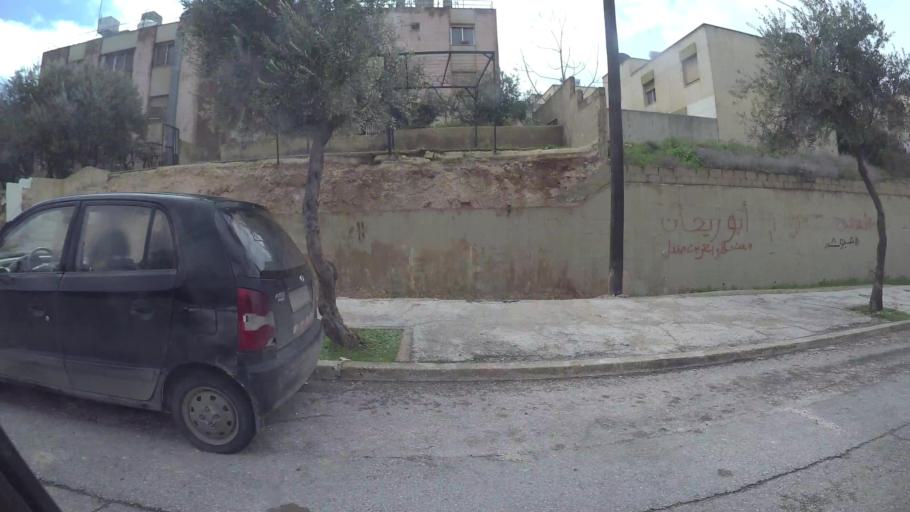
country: JO
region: Amman
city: Al Jubayhah
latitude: 32.0586
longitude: 35.8777
